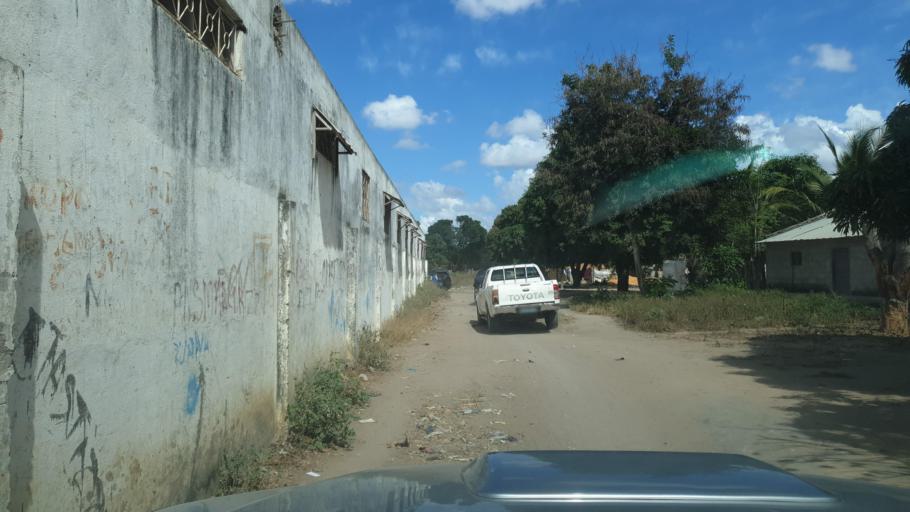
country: MZ
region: Nampula
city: Nacala
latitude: -14.5672
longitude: 40.7007
